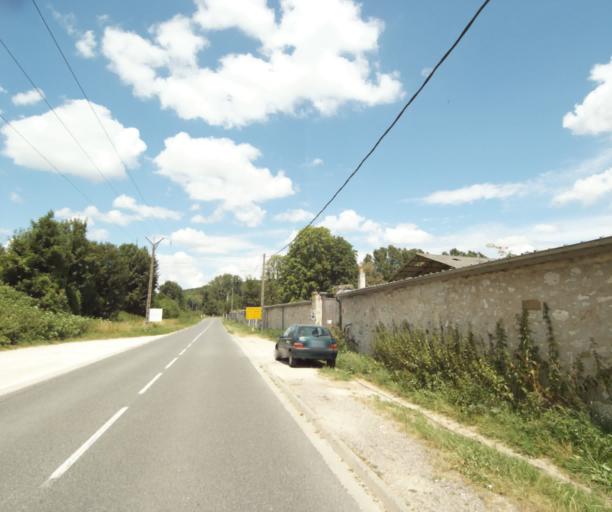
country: FR
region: Ile-de-France
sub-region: Departement de Seine-et-Marne
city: Hericy
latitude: 48.4631
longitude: 2.7730
